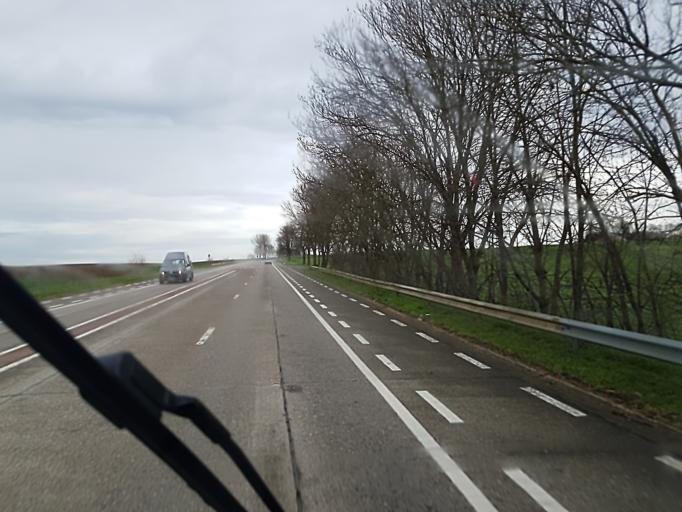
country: BE
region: Wallonia
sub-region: Province de Liege
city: Oreye
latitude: 50.7207
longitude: 5.3189
